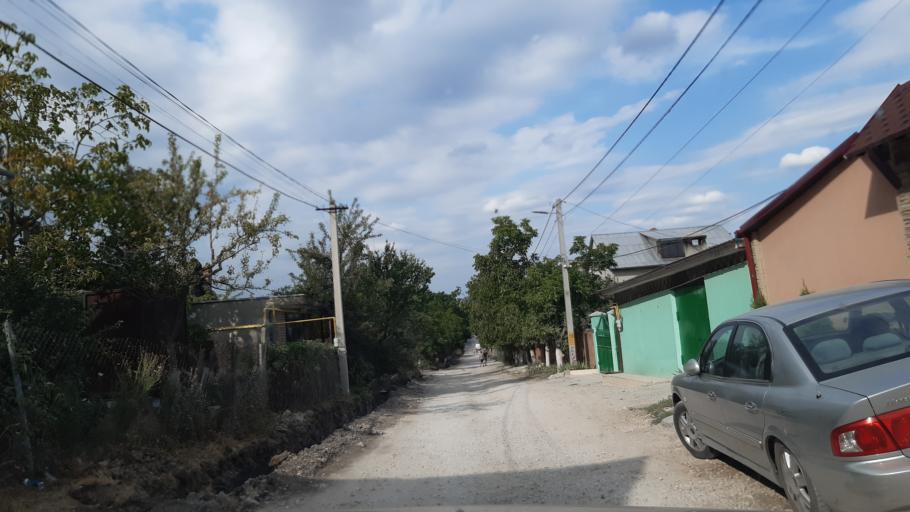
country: MD
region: Chisinau
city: Vatra
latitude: 47.0453
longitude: 28.7354
